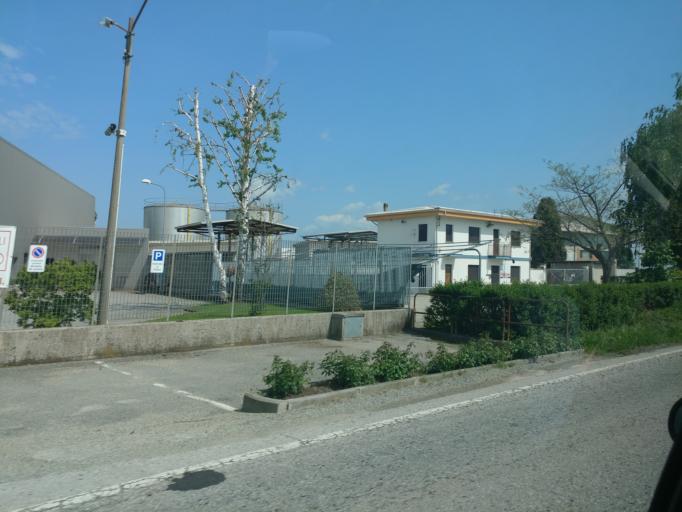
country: IT
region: Piedmont
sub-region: Provincia di Torino
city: Cavour
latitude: 44.7431
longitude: 7.4123
